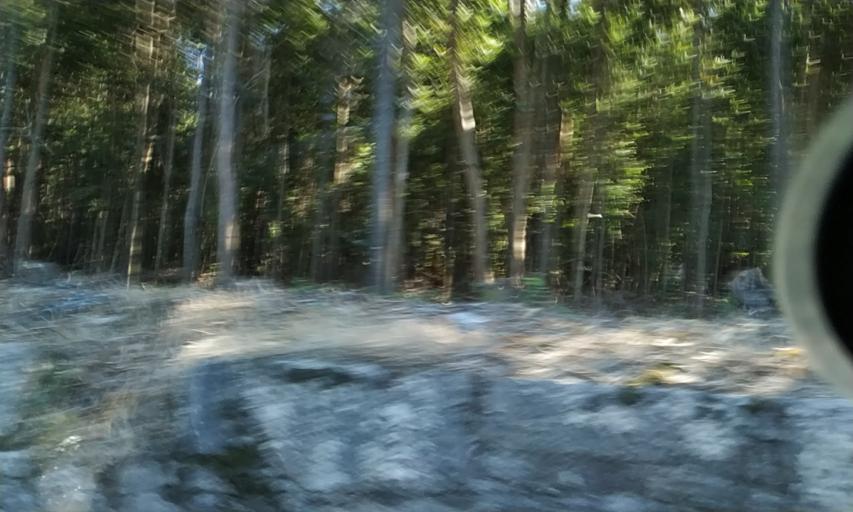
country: PT
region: Porto
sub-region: Maia
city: Anta
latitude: 41.2938
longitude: -8.6166
